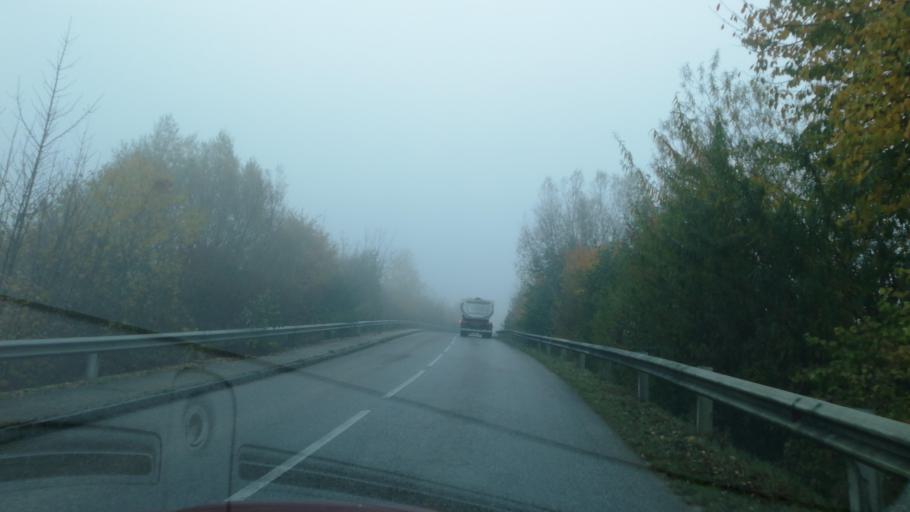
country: AT
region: Upper Austria
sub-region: Politischer Bezirk Grieskirchen
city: Bad Schallerbach
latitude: 48.1826
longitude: 13.9023
